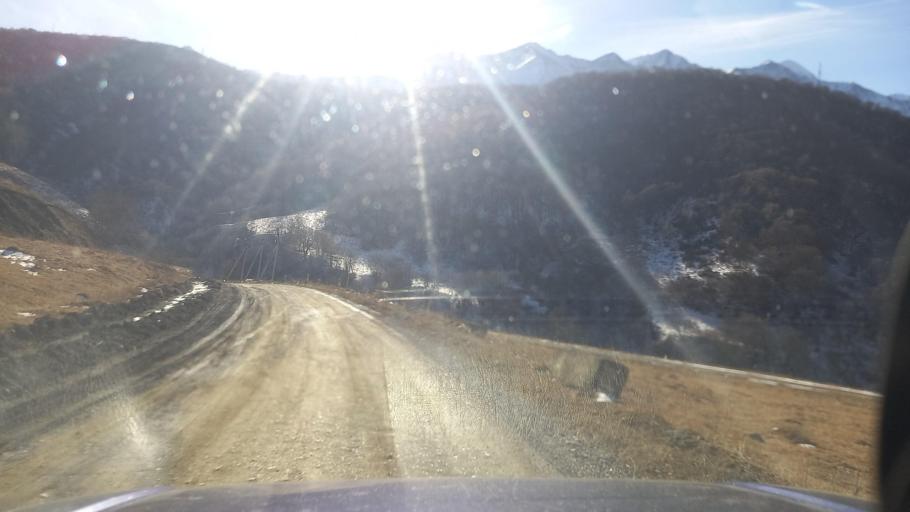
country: RU
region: North Ossetia
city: Verkhniy Fiagdon
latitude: 42.8394
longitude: 44.4638
